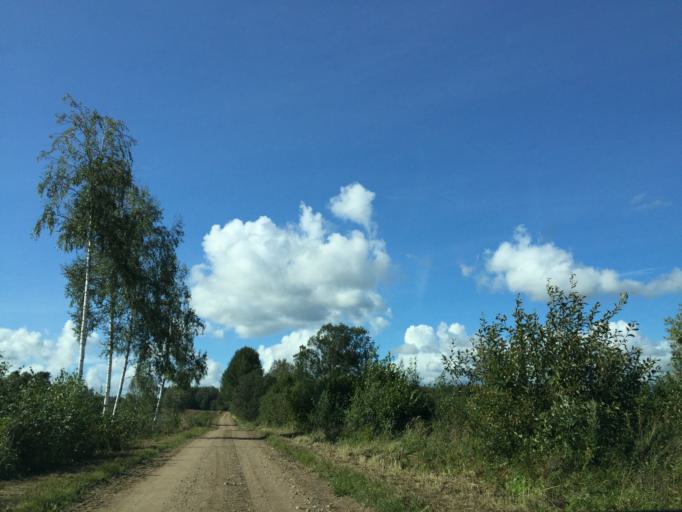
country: LV
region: Kuldigas Rajons
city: Kuldiga
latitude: 56.9950
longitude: 21.8274
